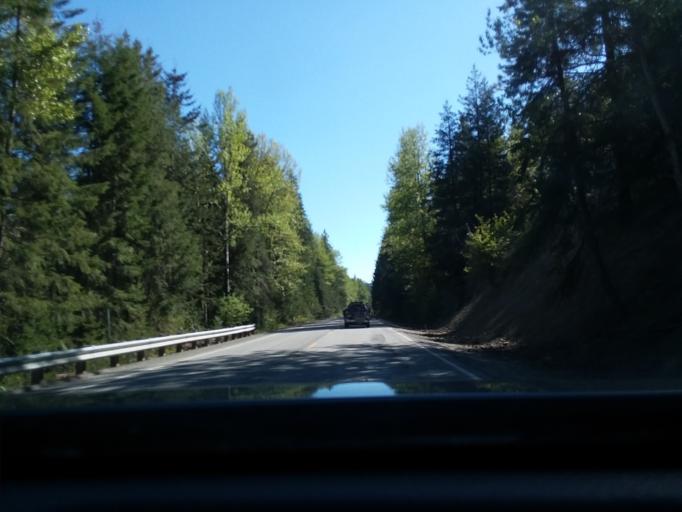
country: US
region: Washington
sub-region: Chelan County
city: Leavenworth
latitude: 47.7878
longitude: -120.6642
